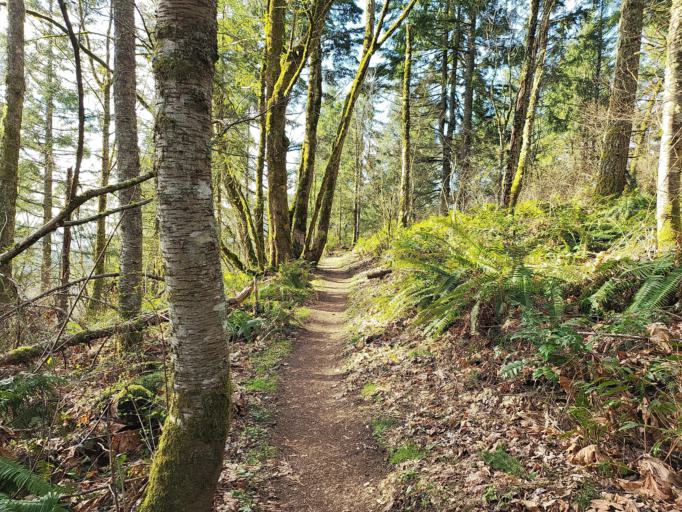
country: US
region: Washington
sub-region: King County
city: Newcastle
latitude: 47.5200
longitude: -122.1259
